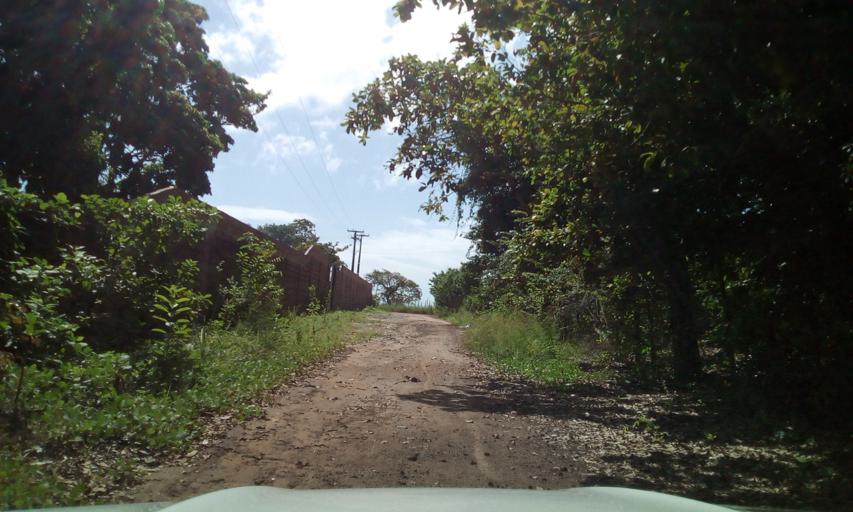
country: BR
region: Paraiba
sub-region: Conde
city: Conde
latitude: -7.2219
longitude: -34.8214
